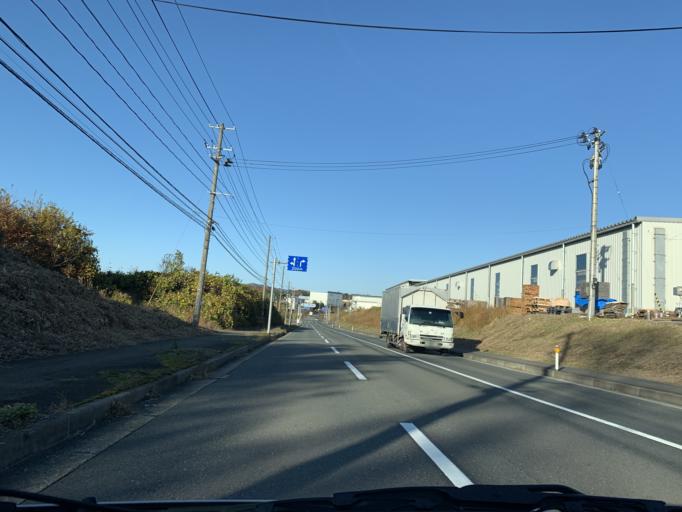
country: JP
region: Iwate
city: Mizusawa
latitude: 39.2058
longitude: 141.1783
